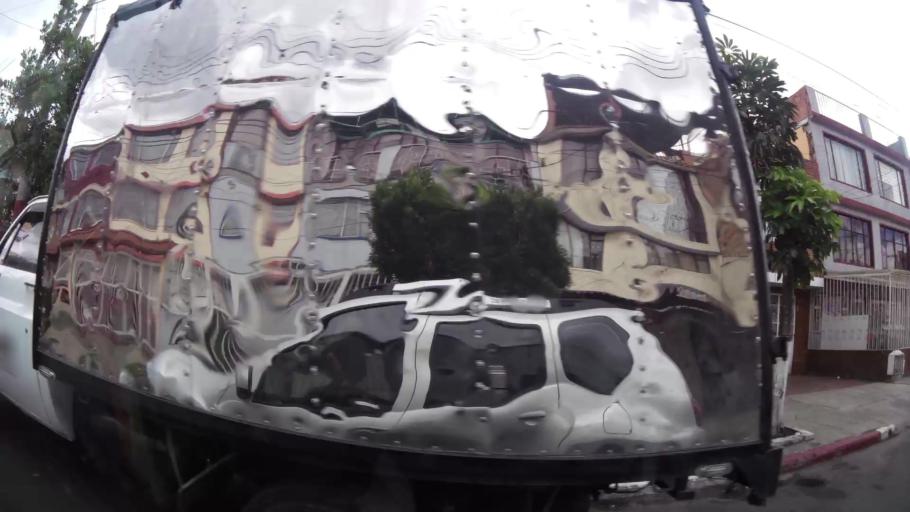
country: CO
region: Bogota D.C.
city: Bogota
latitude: 4.6141
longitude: -74.1220
